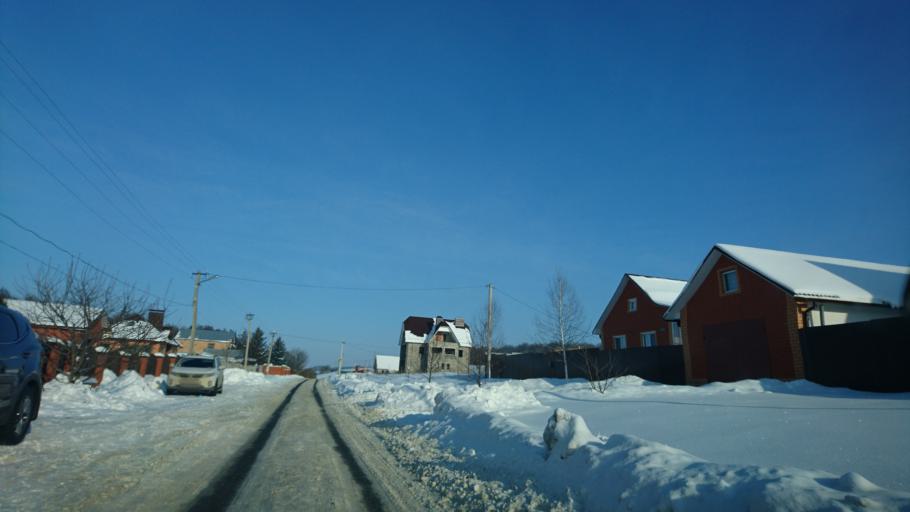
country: RU
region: Belgorod
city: Severnyy
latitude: 50.7234
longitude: 36.6106
